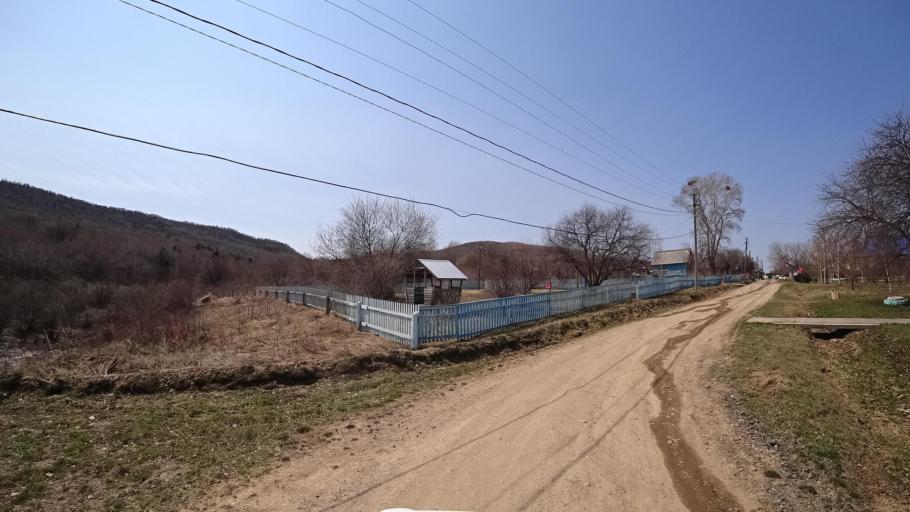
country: RU
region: Khabarovsk Krai
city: Selikhino
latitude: 50.6688
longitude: 137.4005
